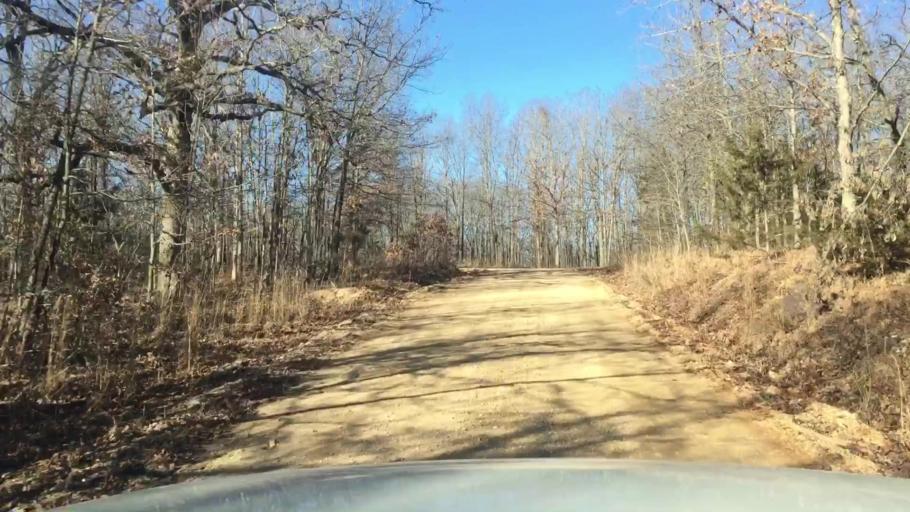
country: US
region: Missouri
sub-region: Morgan County
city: Versailles
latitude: 38.3301
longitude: -92.7718
